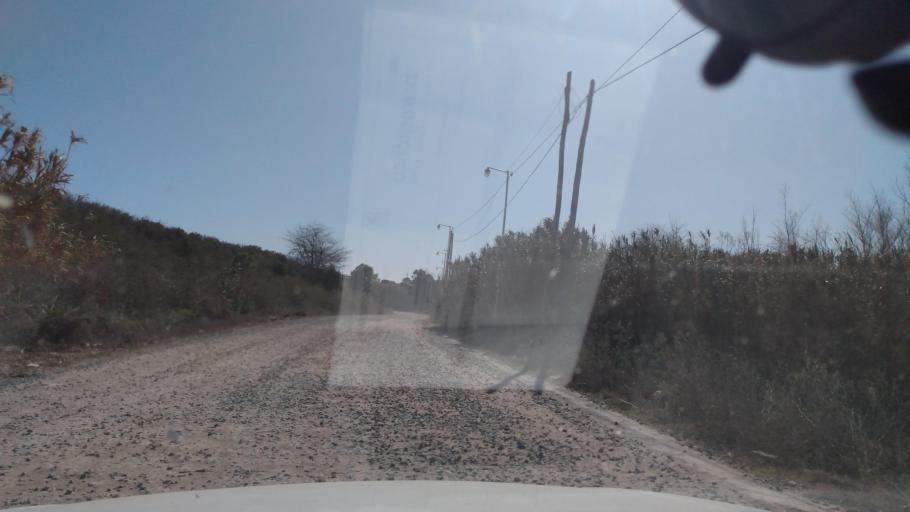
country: AR
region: Buenos Aires
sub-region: Partido de Mercedes
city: Mercedes
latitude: -34.6591
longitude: -59.4005
